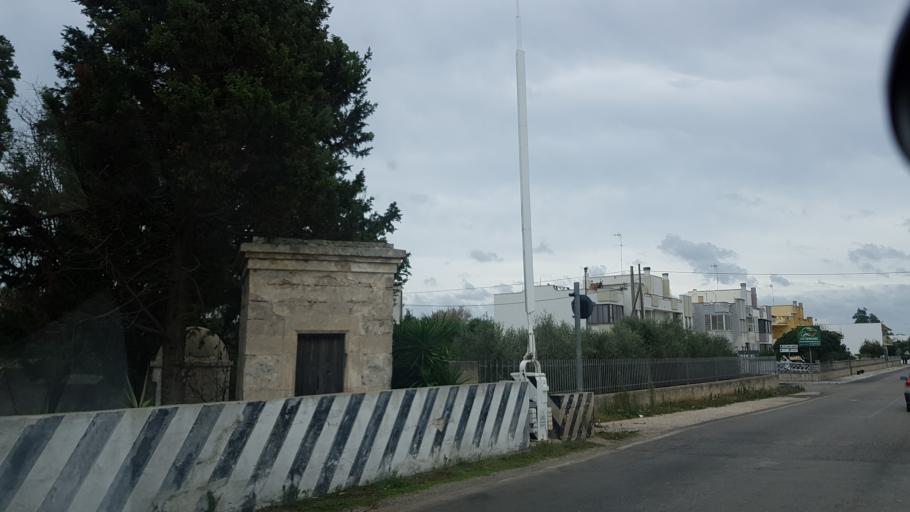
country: IT
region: Apulia
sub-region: Provincia di Lecce
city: Guagnano
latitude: 40.4001
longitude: 17.9408
